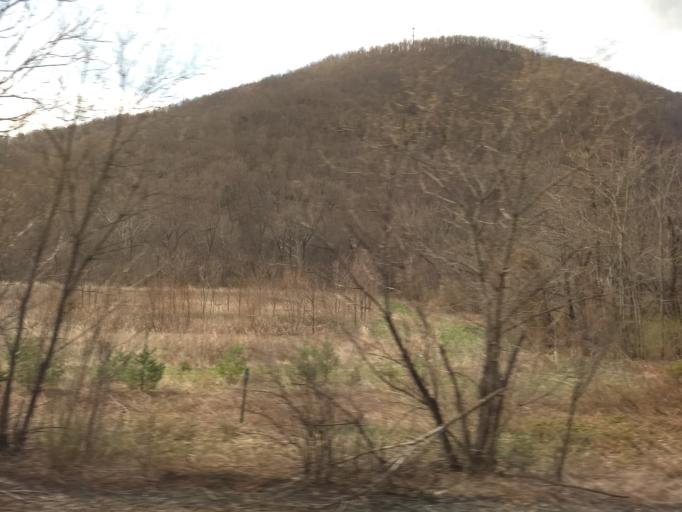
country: US
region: Pennsylvania
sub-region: Huntingdon County
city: Huntingdon
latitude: 40.4455
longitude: -77.9554
